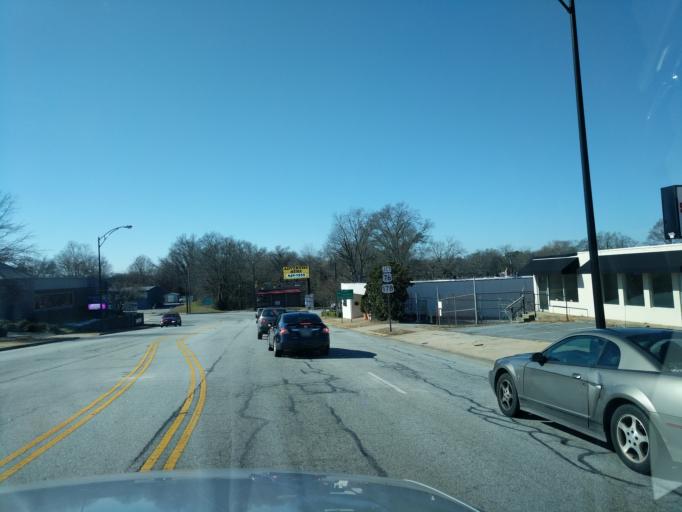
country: US
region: South Carolina
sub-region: Anderson County
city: Anderson
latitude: 34.5109
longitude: -82.6493
